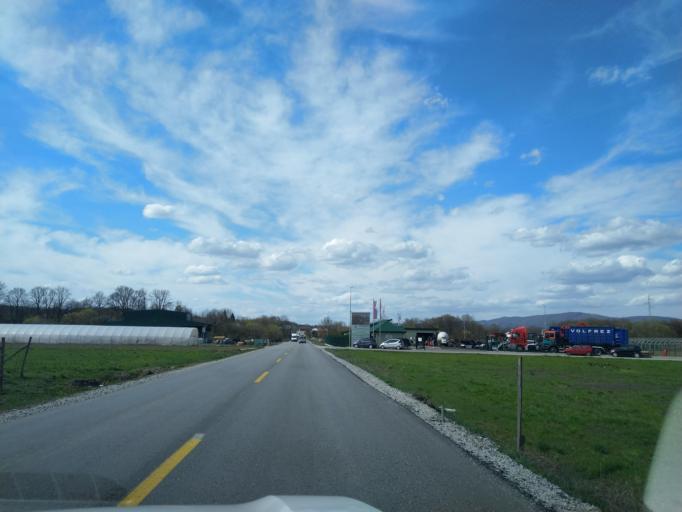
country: RS
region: Central Serbia
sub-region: Zlatiborski Okrug
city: Arilje
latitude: 43.7903
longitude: 20.1041
